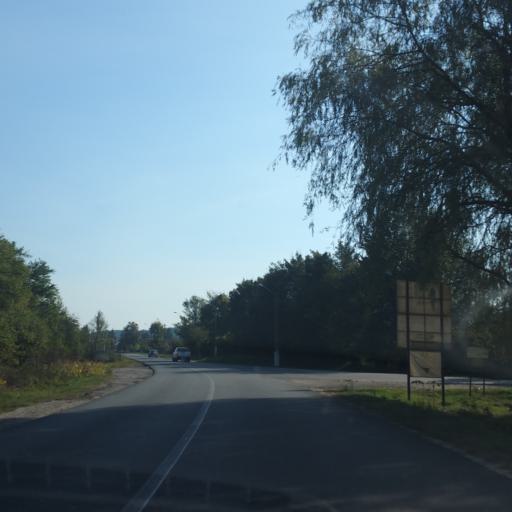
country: RO
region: Arges
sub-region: Comuna Merisani
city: Merisani
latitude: 44.9701
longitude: 24.7466
